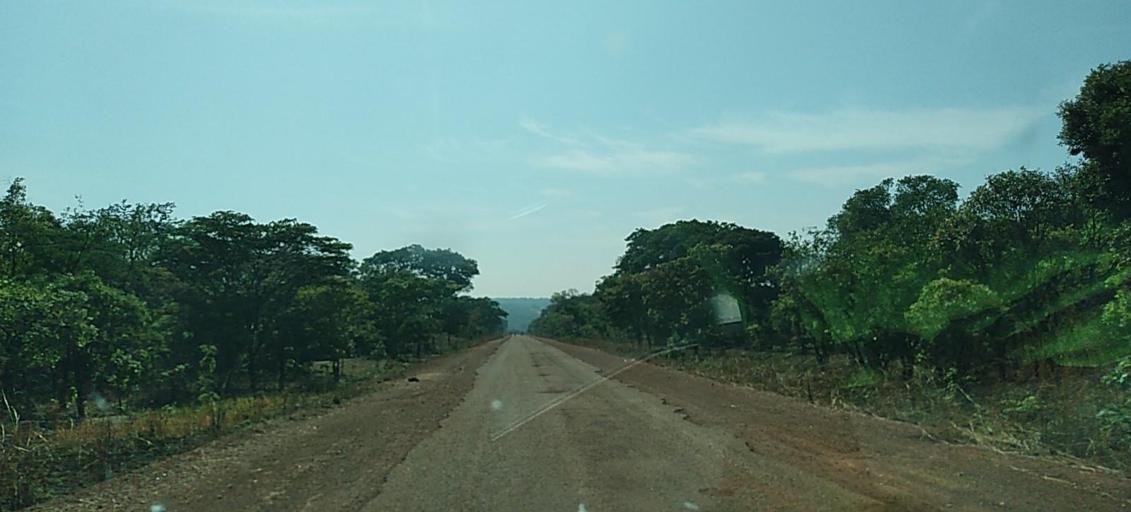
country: ZM
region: North-Western
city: Mwinilunga
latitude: -11.8229
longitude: 25.1120
